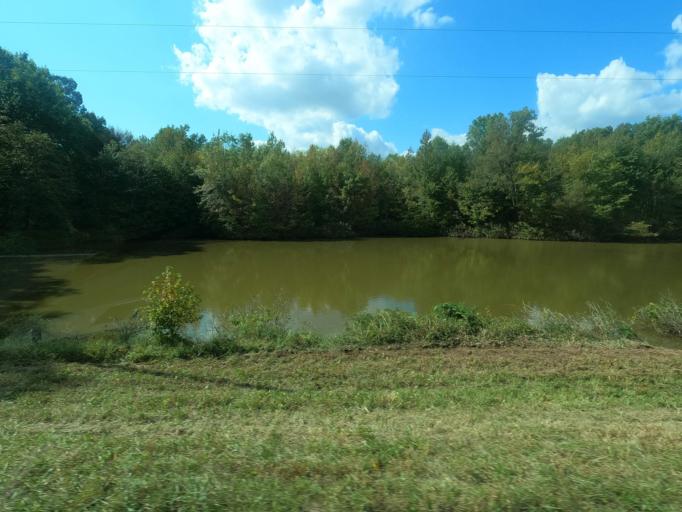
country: US
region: Illinois
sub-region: Massac County
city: Metropolis
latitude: 37.2871
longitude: -88.7571
